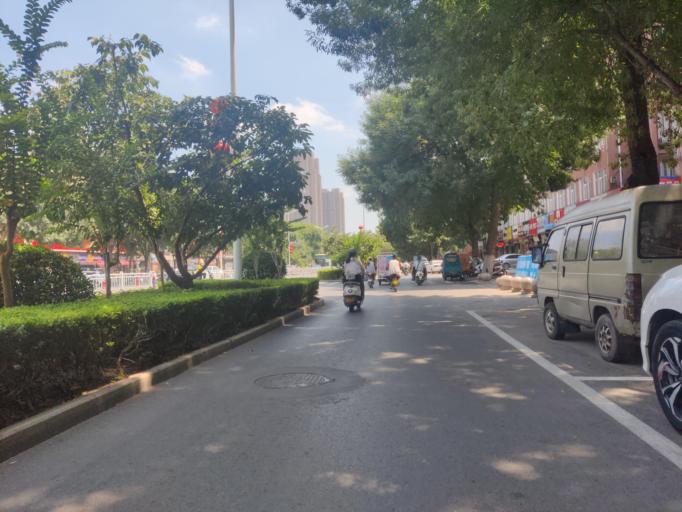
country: CN
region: Henan Sheng
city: Puyang
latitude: 35.7722
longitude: 115.0286
